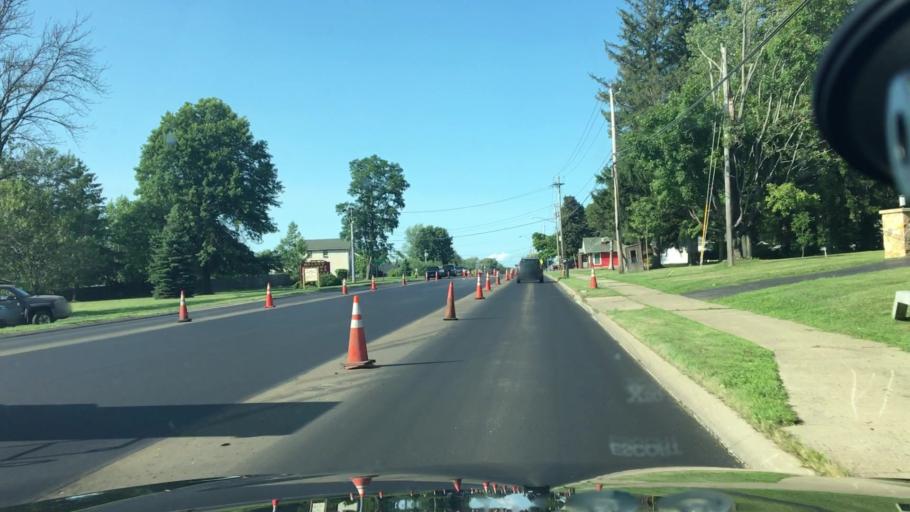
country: US
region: New York
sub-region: Erie County
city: Angola on the Lake
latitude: 42.6411
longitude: -79.0463
